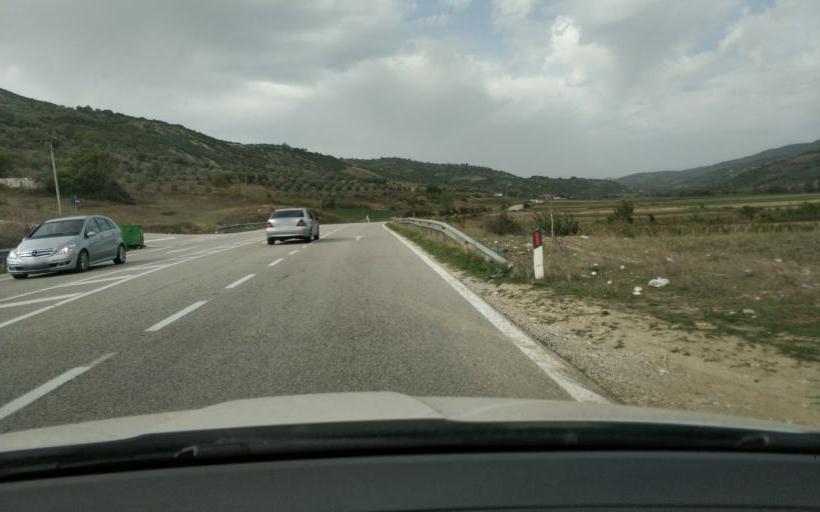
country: AL
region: Gjirokaster
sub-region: Rrethi i Tepelenes
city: Krahes
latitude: 40.4402
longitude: 19.8489
